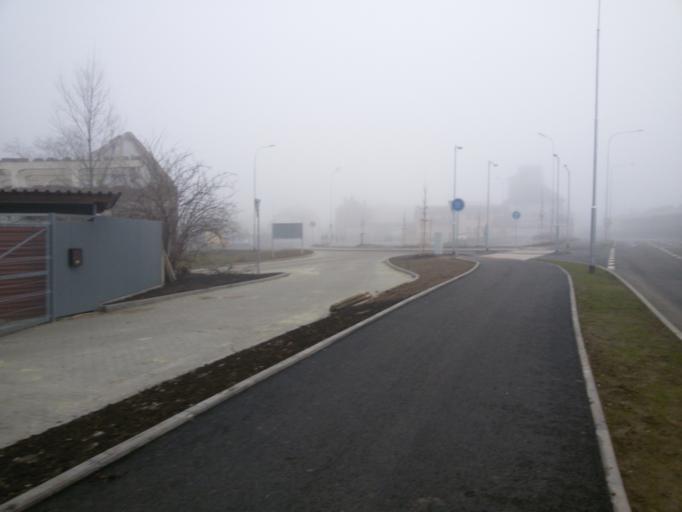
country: CZ
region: South Moravian
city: Tisnov
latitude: 49.3497
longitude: 16.4164
